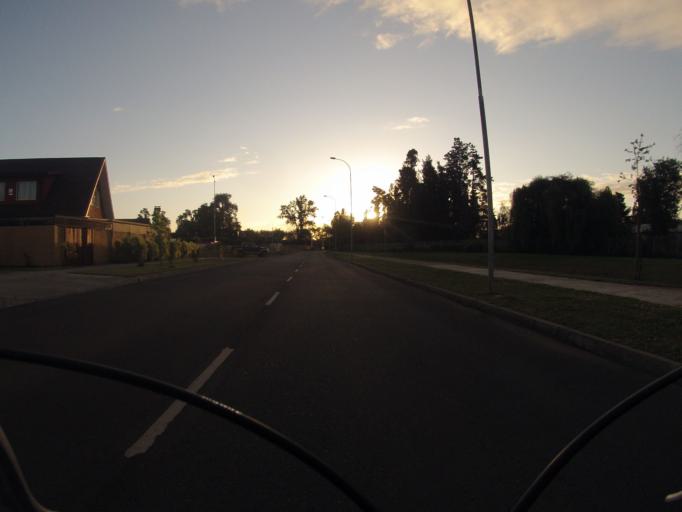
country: CL
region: Araucania
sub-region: Provincia de Cautin
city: Temuco
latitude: -38.7377
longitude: -72.6492
